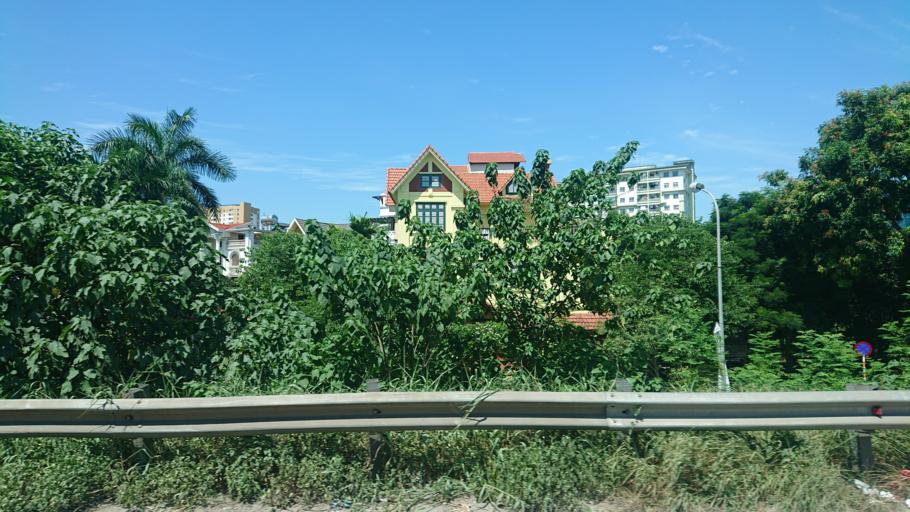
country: VN
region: Ha Noi
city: Van Dien
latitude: 20.9612
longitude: 105.8474
